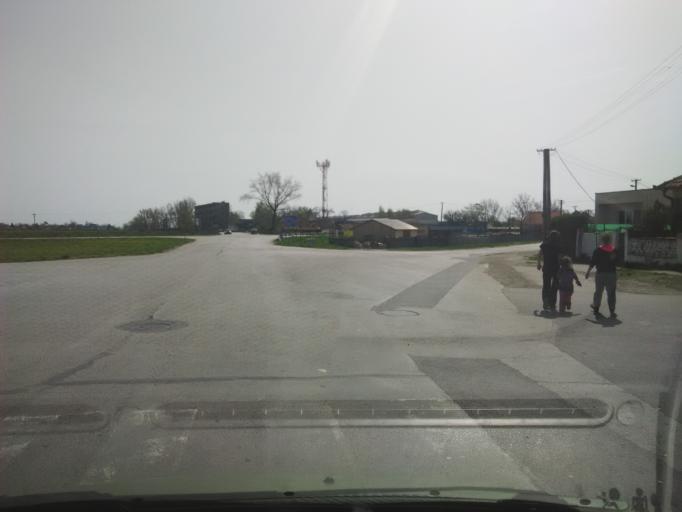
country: SK
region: Bratislavsky
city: Senec
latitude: 48.1249
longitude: 17.4227
